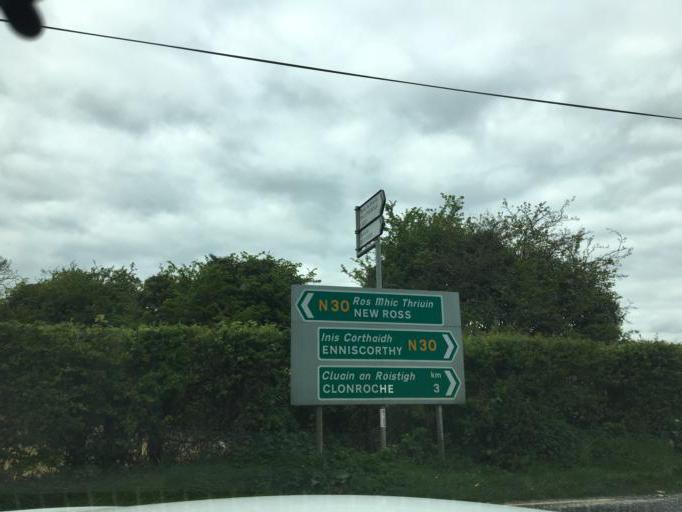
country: IE
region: Leinster
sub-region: Loch Garman
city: New Ross
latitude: 52.4354
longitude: -6.7444
